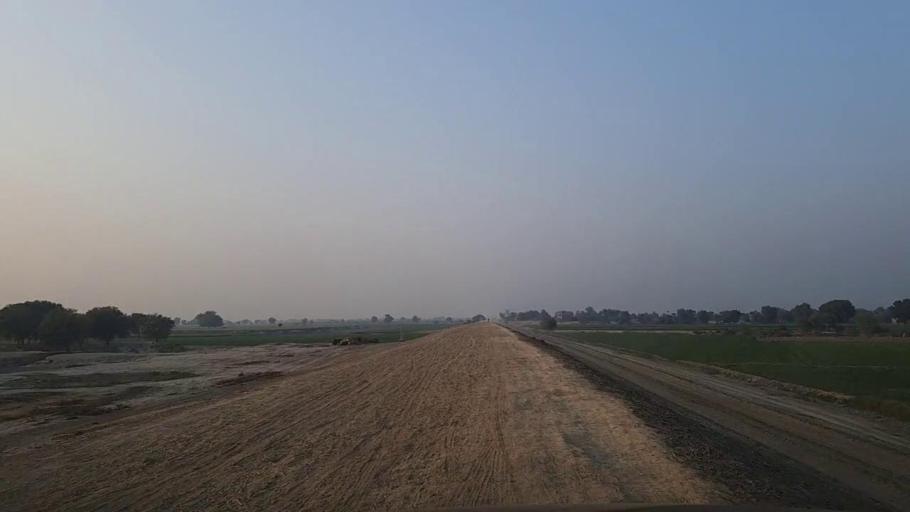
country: PK
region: Sindh
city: Sann
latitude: 26.1889
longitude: 68.0918
